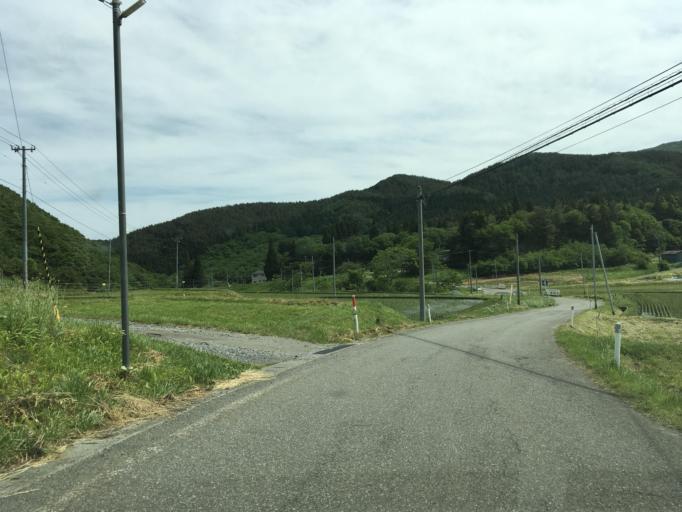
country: JP
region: Iwate
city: Mizusawa
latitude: 39.1092
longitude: 141.3280
